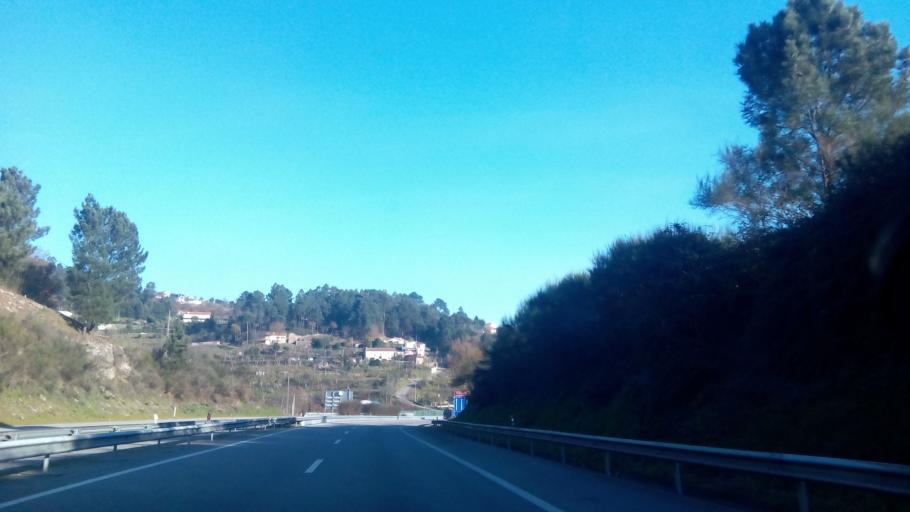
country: PT
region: Porto
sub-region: Marco de Canaveses
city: Marco de Canavezes
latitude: 41.2212
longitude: -8.1629
